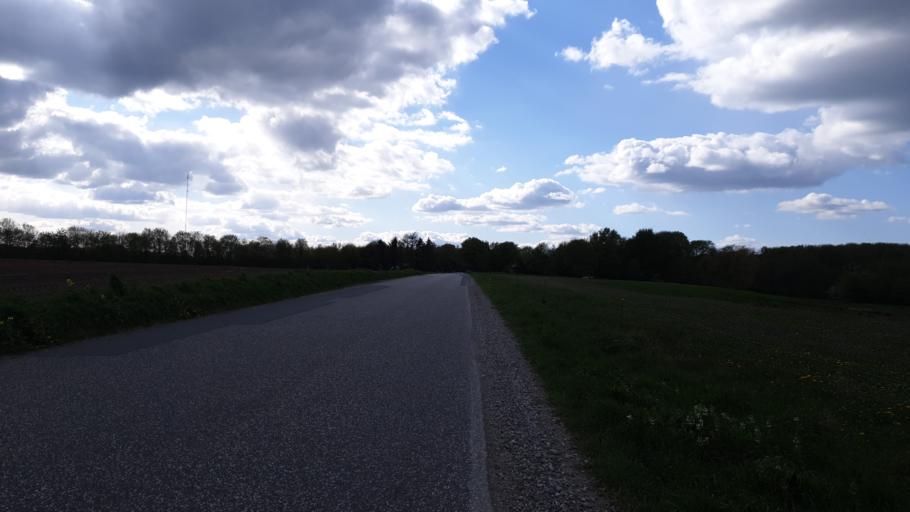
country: DK
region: Central Jutland
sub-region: Hedensted Kommune
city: Hedensted
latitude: 55.8113
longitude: 9.6652
